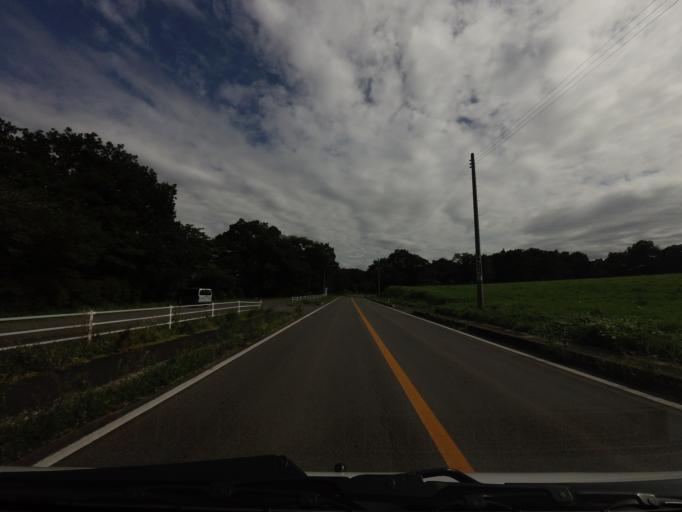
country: JP
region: Fukushima
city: Nihommatsu
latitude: 37.6102
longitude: 140.3590
